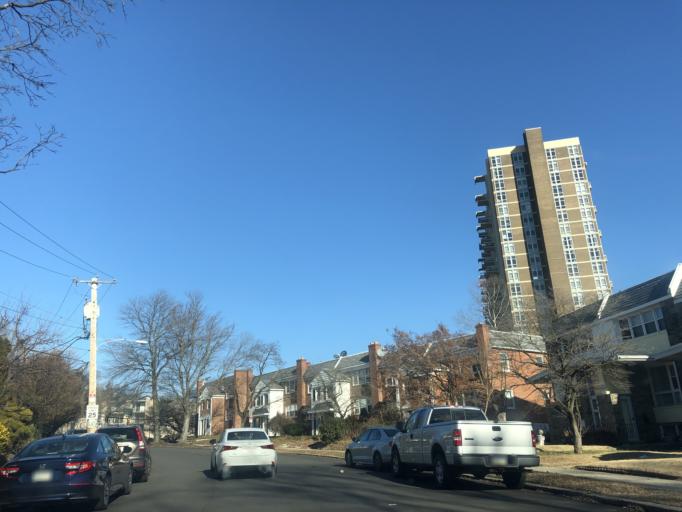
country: US
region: Pennsylvania
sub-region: Montgomery County
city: Bala-Cynwyd
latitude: 40.0026
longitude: -75.2030
